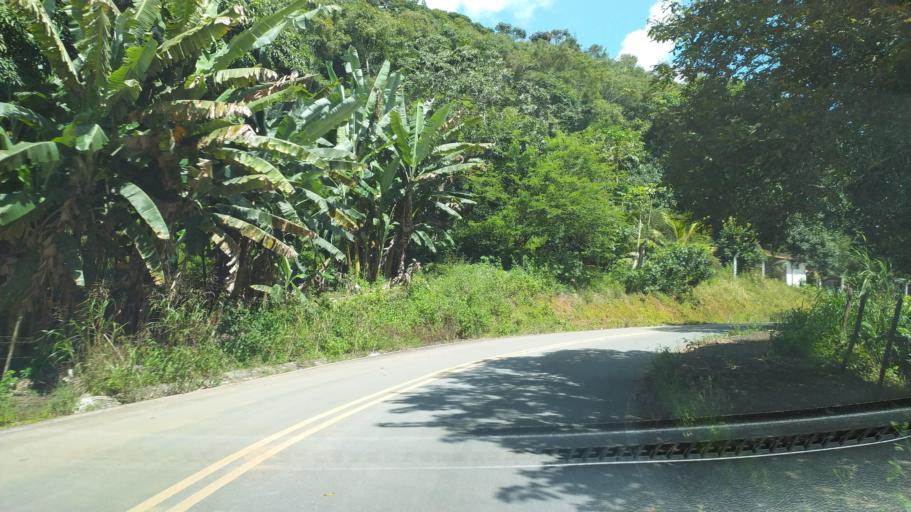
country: BR
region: Alagoas
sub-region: Uniao Dos Palmares
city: Uniao dos Palmares
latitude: -9.1634
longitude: -36.0721
